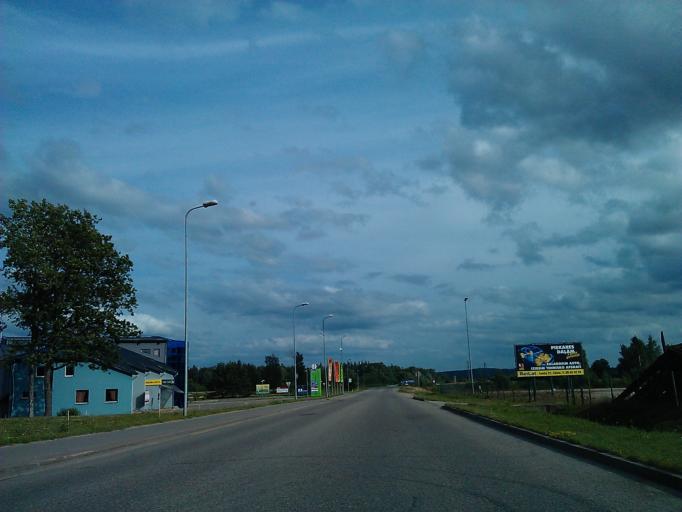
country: LV
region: Cesu Rajons
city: Cesis
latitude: 57.2974
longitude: 25.3012
